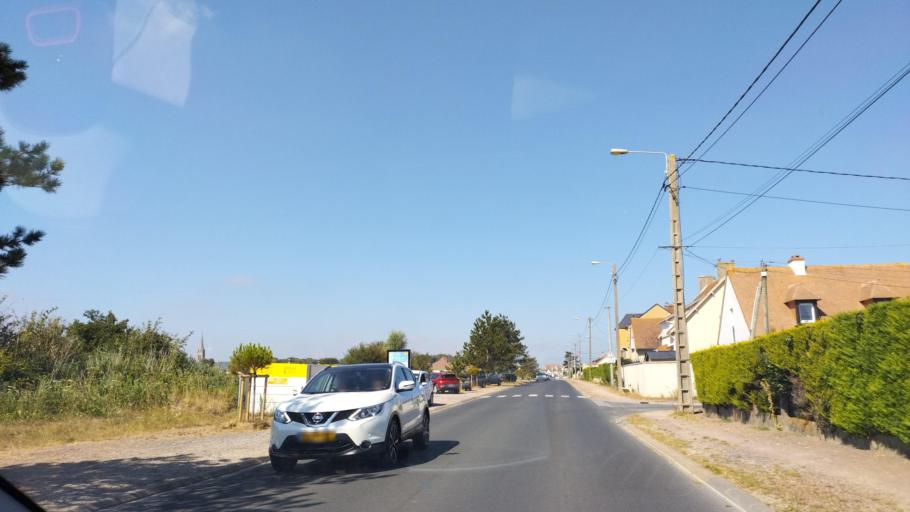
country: FR
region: Lower Normandy
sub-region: Departement du Calvados
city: Bernieres-sur-Mer
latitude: 49.3345
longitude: -0.4121
